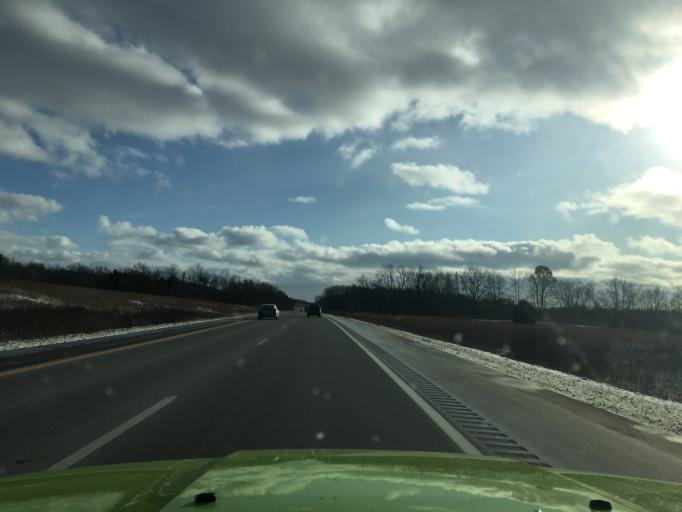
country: US
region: Michigan
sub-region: Kent County
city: Cedar Springs
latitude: 43.1962
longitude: -85.5778
